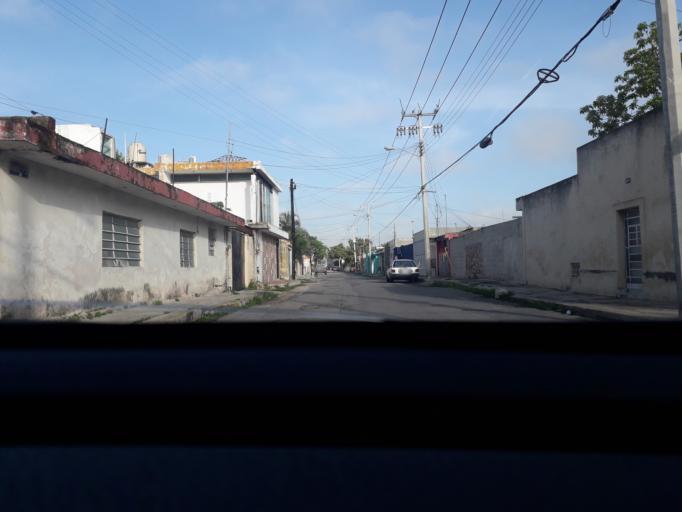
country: MX
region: Yucatan
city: Merida
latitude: 20.9609
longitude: -89.6338
